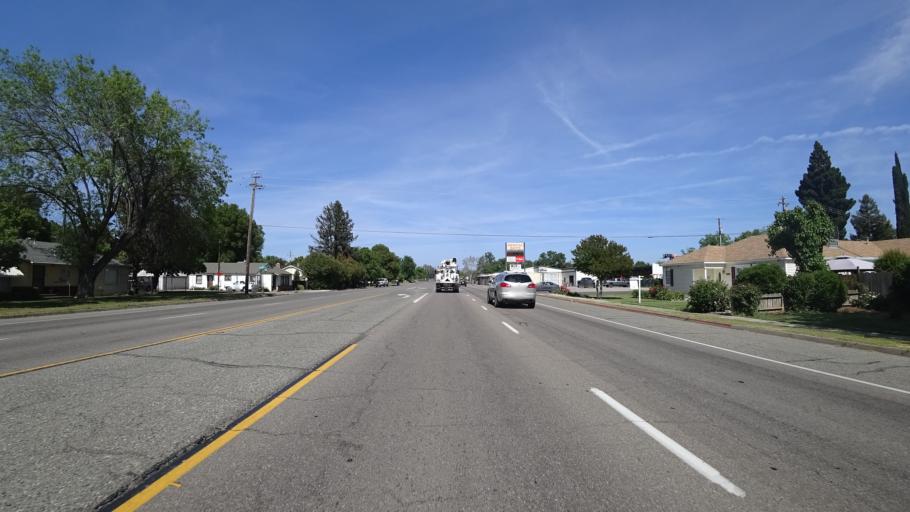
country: US
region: California
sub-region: Tehama County
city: Red Bluff
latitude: 40.1845
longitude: -122.2166
